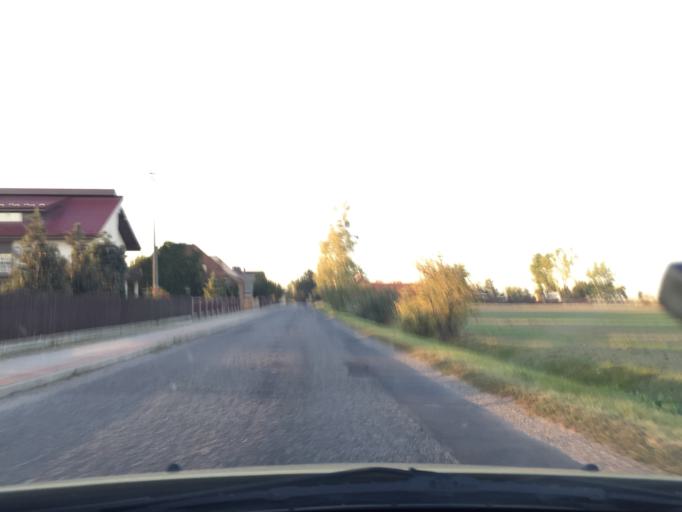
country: PL
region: Greater Poland Voivodeship
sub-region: Powiat pleszewski
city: Dobrzyca
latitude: 51.8171
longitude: 17.6214
